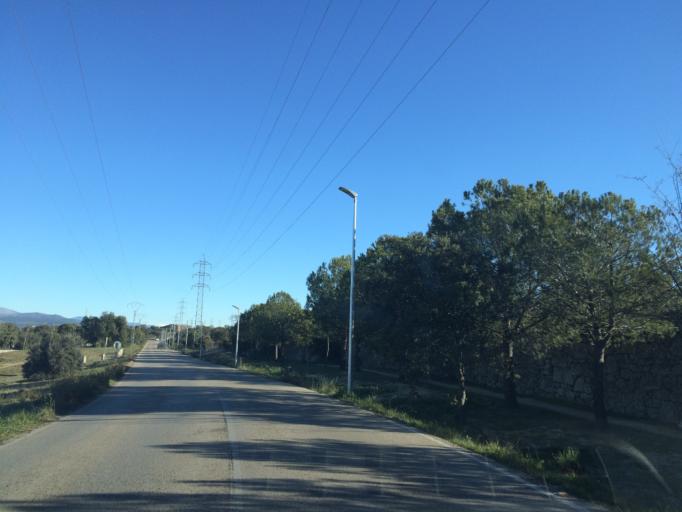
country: ES
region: Madrid
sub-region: Provincia de Madrid
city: Tres Cantos
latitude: 40.5974
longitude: -3.6922
